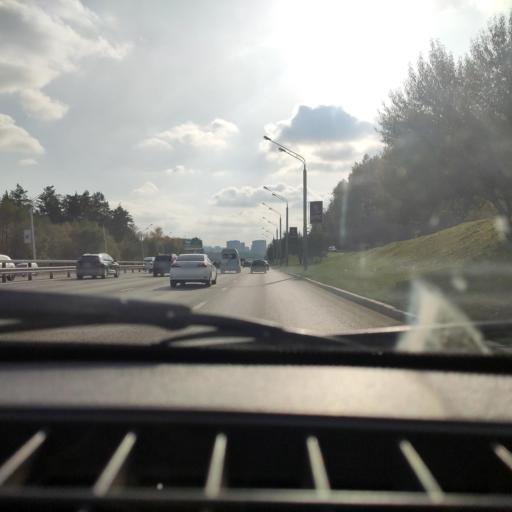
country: RU
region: Bashkortostan
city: Ufa
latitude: 54.7452
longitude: 56.0123
